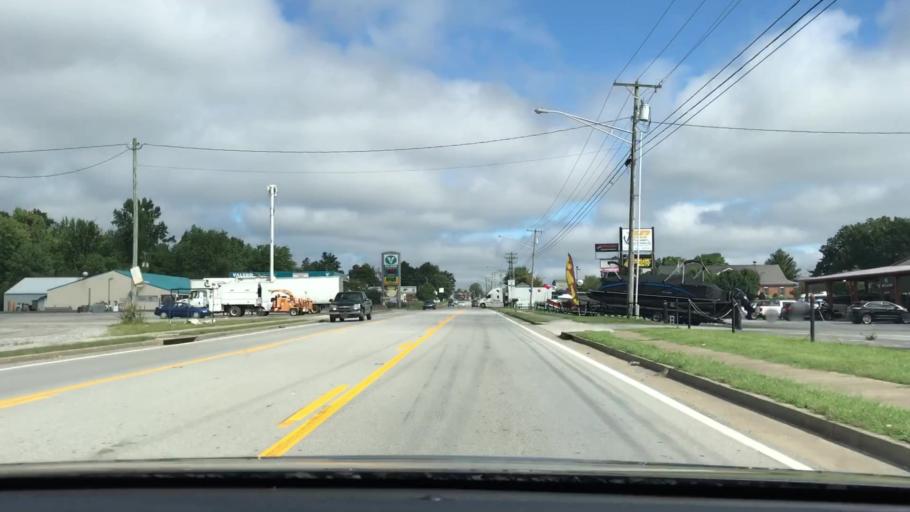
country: US
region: Kentucky
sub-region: Russell County
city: Russell Springs
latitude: 37.0284
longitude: -85.0772
